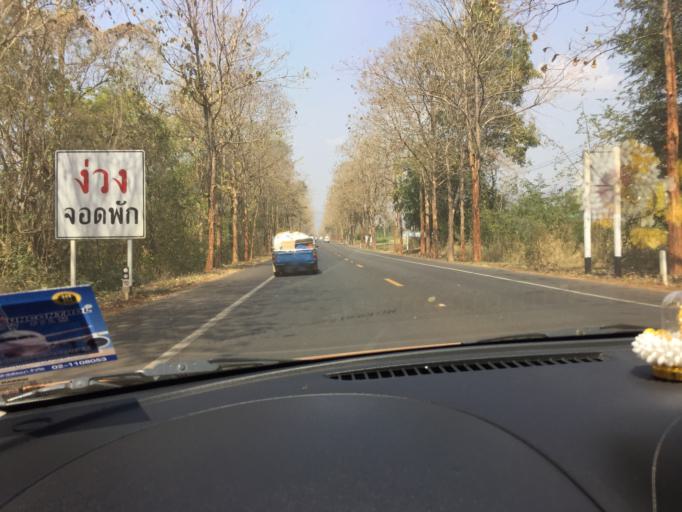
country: TH
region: Kanchanaburi
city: Sai Yok
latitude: 14.1775
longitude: 99.1271
